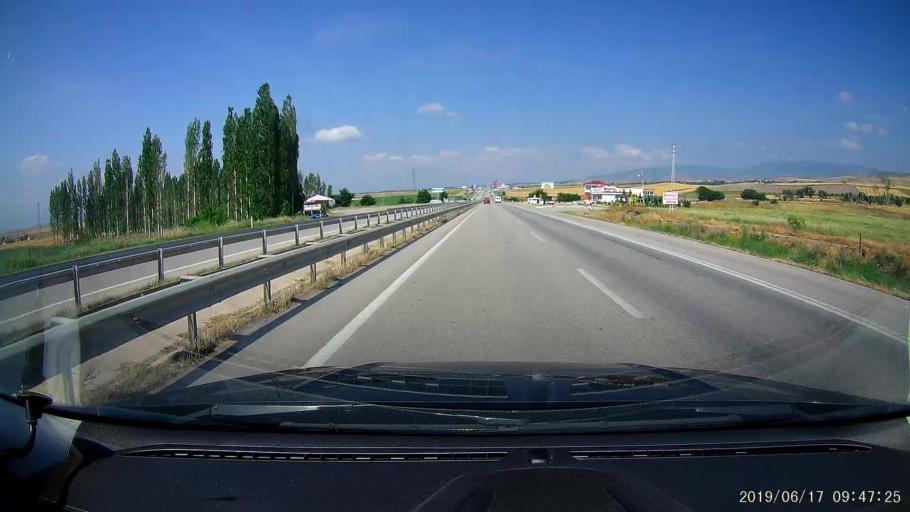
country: TR
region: Amasya
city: Suluova
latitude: 40.8766
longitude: 35.5787
